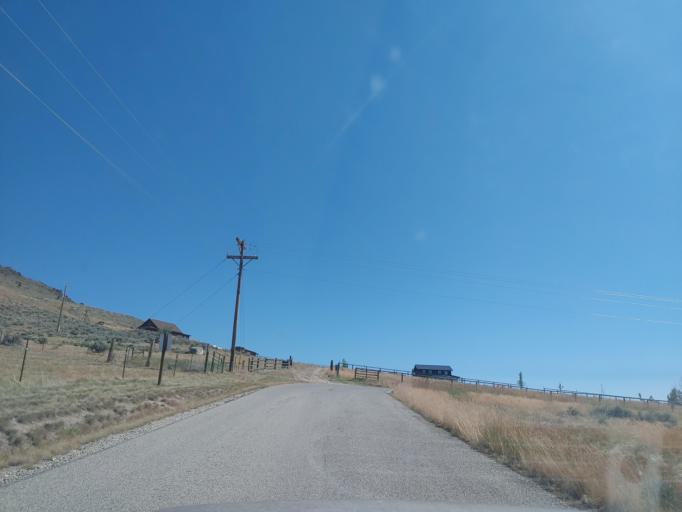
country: US
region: Montana
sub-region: Ravalli County
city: Hamilton
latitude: 46.3495
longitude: -114.0378
